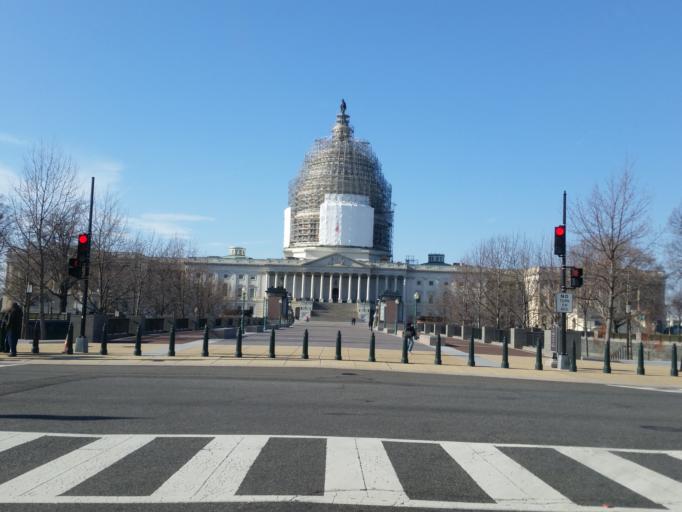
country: US
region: Washington, D.C.
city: Washington, D.C.
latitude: 38.8899
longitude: -77.0058
